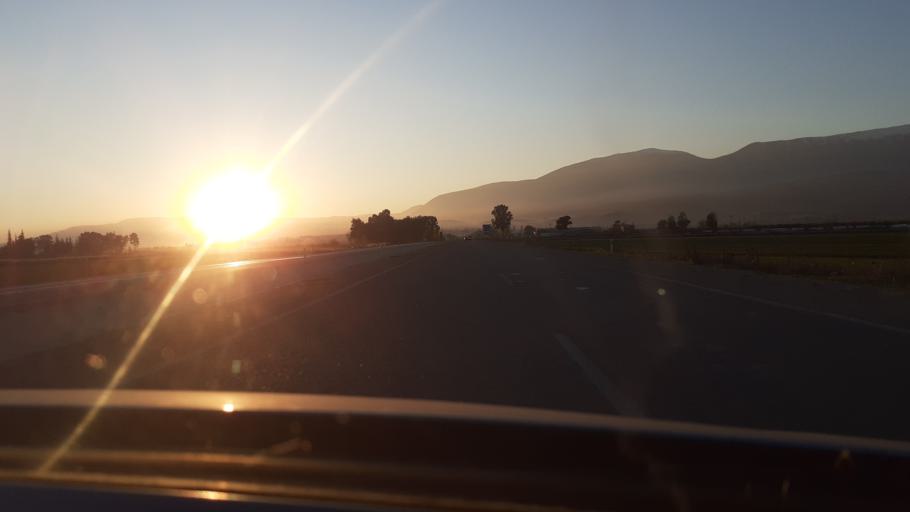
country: TR
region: Hatay
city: Kirikhan
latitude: 36.5059
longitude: 36.4212
